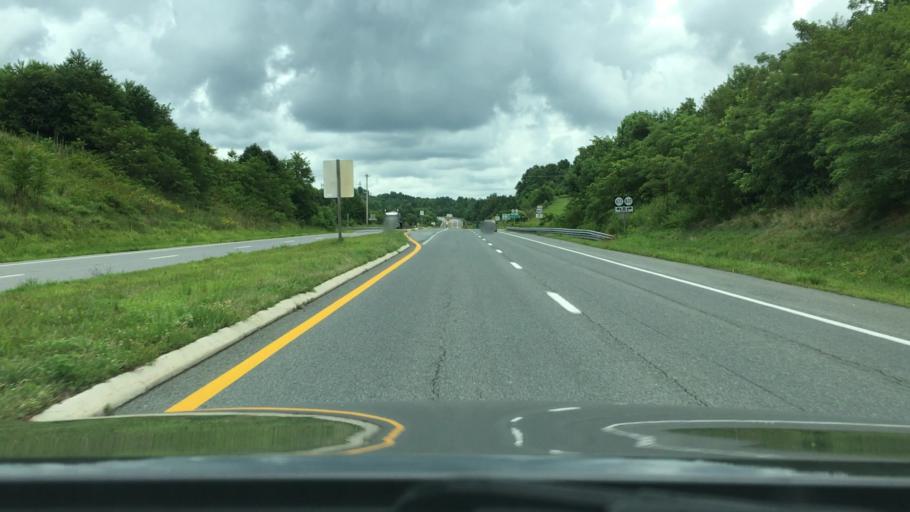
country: US
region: Virginia
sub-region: Amherst County
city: Madison Heights
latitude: 37.4104
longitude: -79.0907
